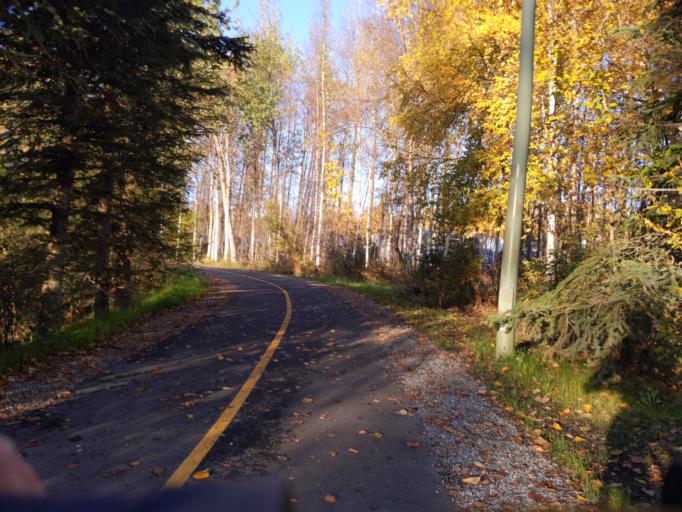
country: US
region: Alaska
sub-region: Anchorage Municipality
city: Anchorage
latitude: 61.1533
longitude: -149.8787
